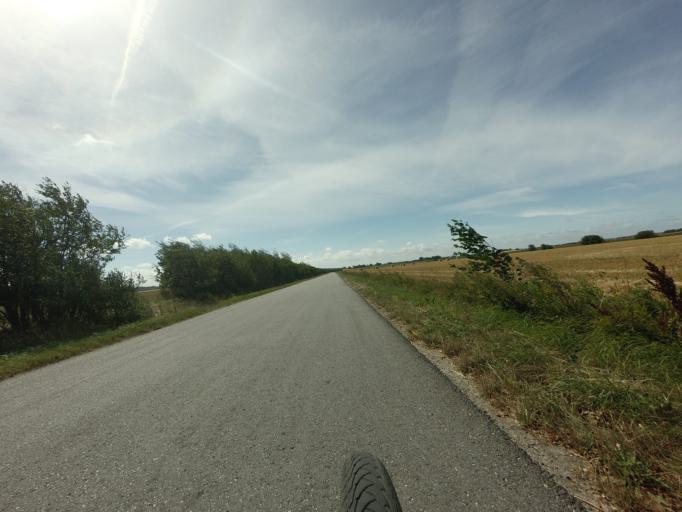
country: DK
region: North Denmark
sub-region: Bronderslev Kommune
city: Bronderslev
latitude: 57.3192
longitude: 9.8149
